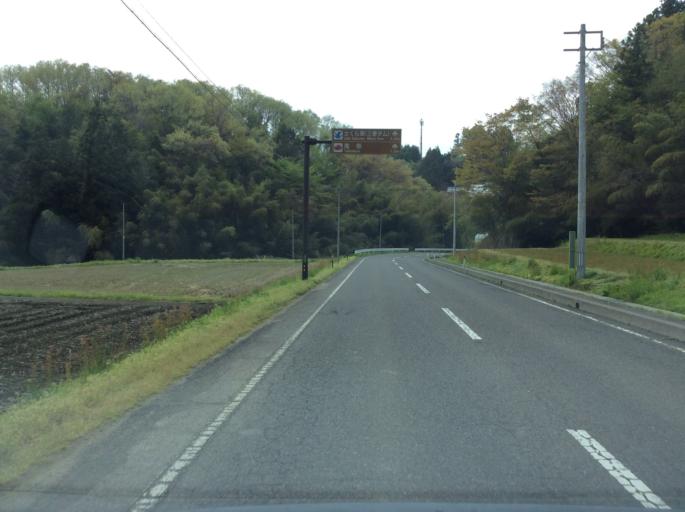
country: JP
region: Fukushima
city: Miharu
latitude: 37.3962
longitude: 140.5065
